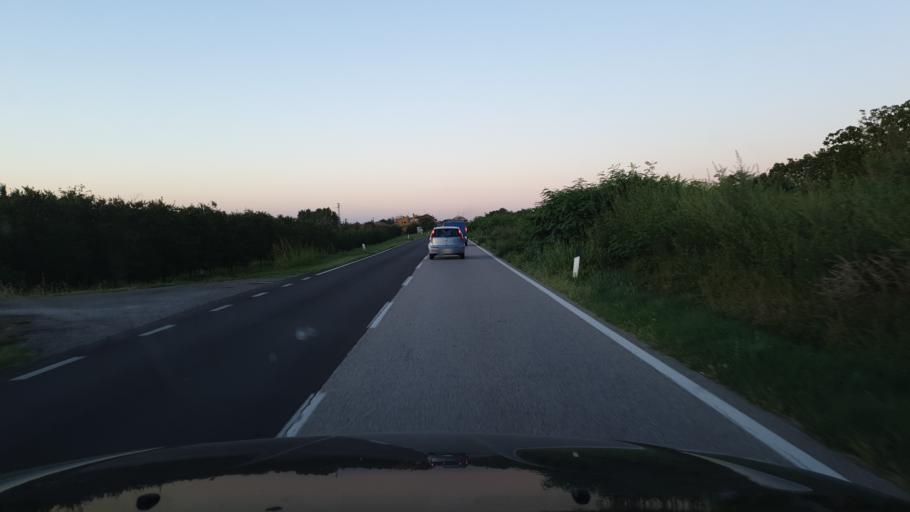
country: IT
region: Emilia-Romagna
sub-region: Provincia di Bologna
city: Ca De Fabbri
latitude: 44.6144
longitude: 11.4501
